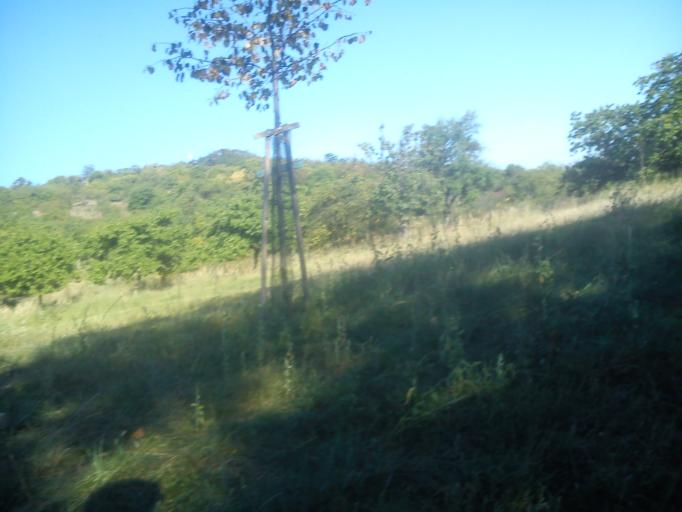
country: CZ
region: South Moravian
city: Sokolnice
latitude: 49.1132
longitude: 16.7639
